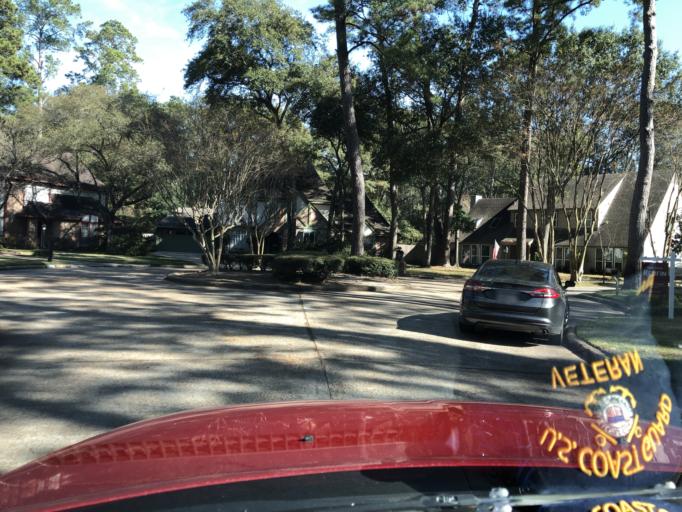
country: US
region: Texas
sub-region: Harris County
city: Tomball
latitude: 30.0258
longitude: -95.5490
